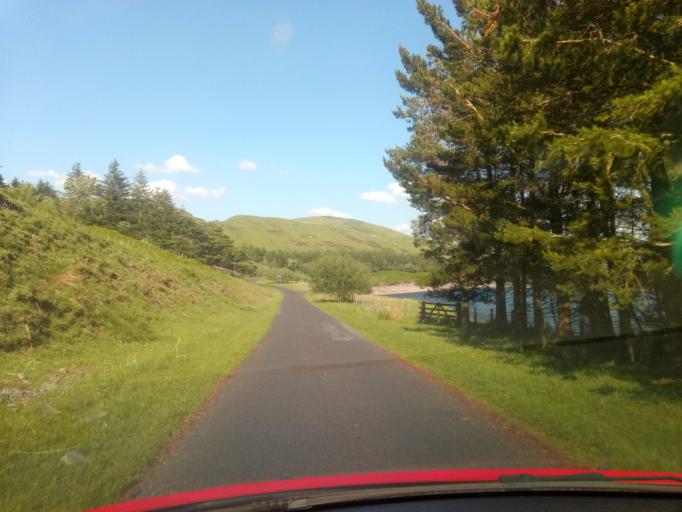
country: GB
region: Scotland
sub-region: The Scottish Borders
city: Peebles
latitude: 55.4953
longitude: -3.2614
